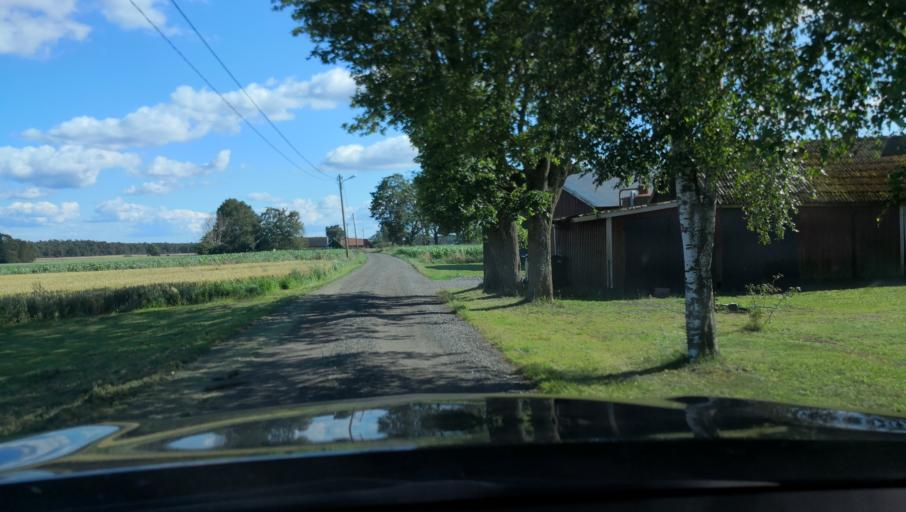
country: SE
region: Skane
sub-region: Kristianstads Kommun
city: Degeberga
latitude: 55.8118
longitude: 14.1890
